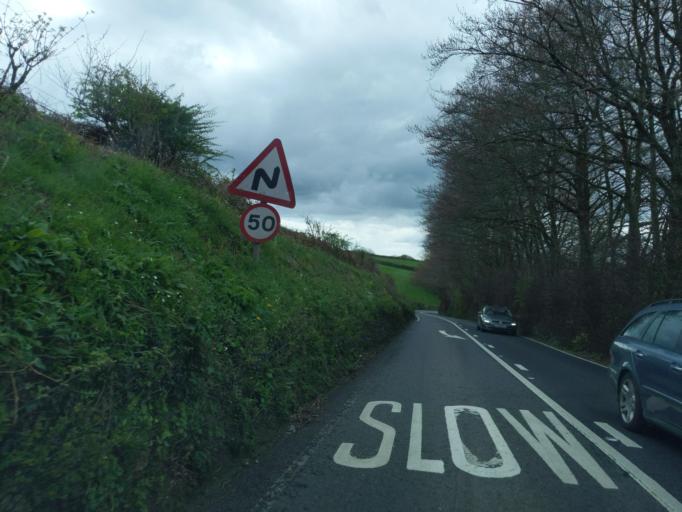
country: GB
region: England
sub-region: Cornwall
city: Pensilva
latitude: 50.4749
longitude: -4.3972
